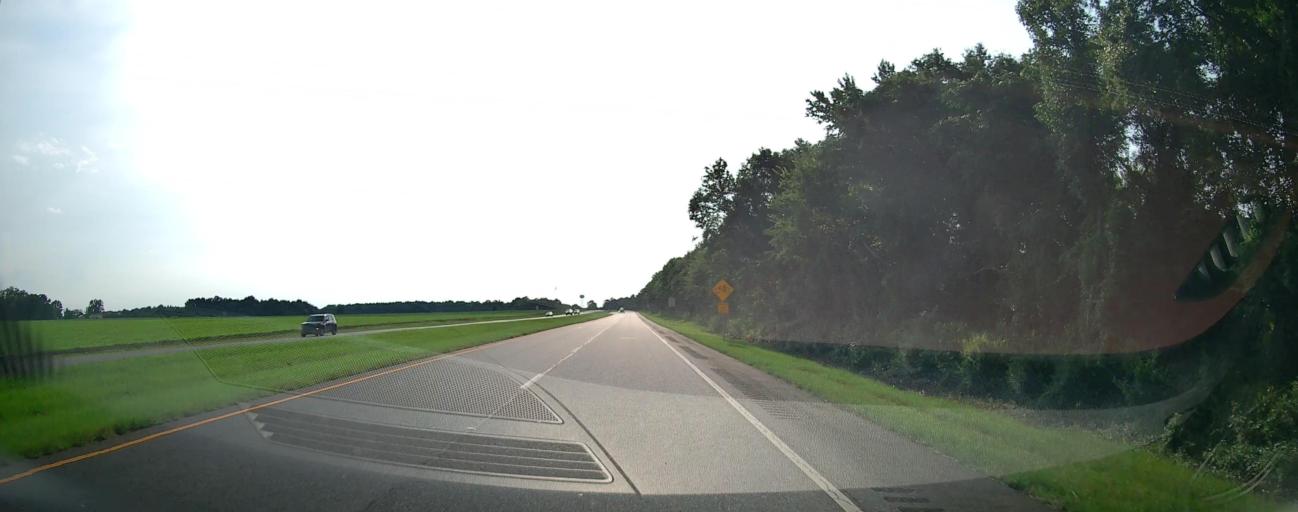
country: US
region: Georgia
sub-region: Taylor County
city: Reynolds
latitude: 32.5585
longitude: -84.0725
